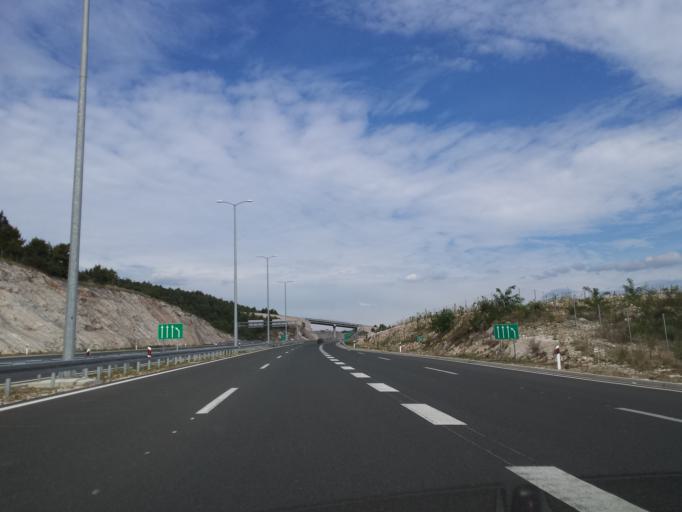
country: BA
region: Federation of Bosnia and Herzegovina
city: Ljubuski
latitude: 43.1523
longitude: 17.4816
